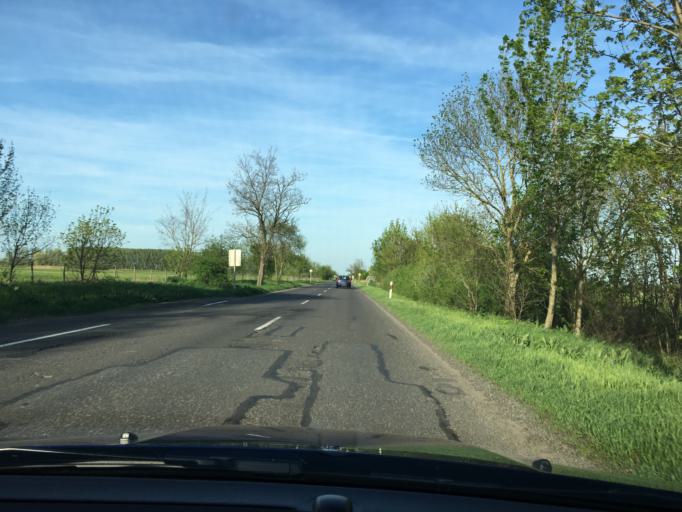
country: HU
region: Hajdu-Bihar
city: Csokmo
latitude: 47.0096
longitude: 21.2402
